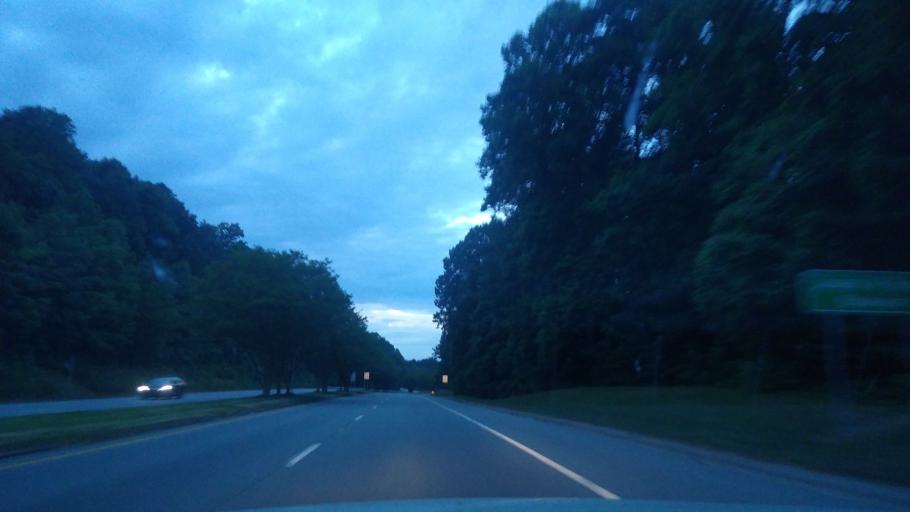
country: US
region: North Carolina
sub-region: Guilford County
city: Greensboro
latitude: 36.0993
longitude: -79.8338
